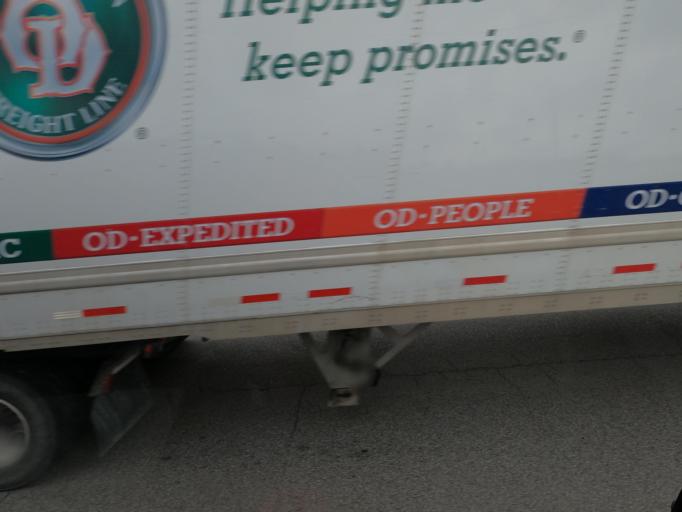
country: US
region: Iowa
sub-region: Wapello County
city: Ottumwa
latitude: 40.9647
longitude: -92.2365
